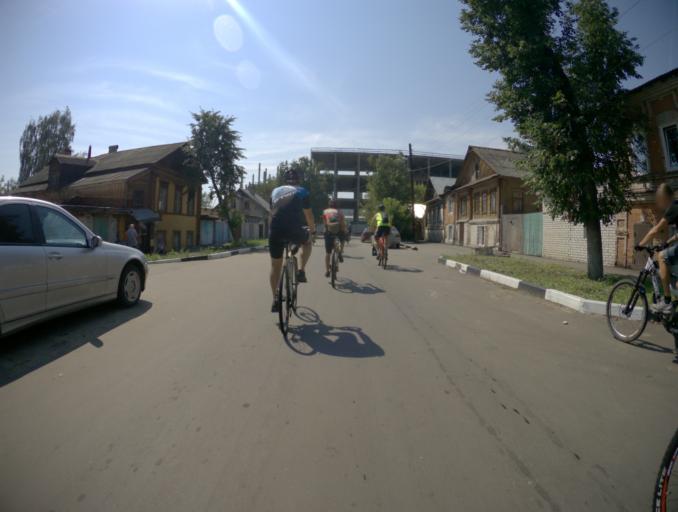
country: RU
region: Nizjnij Novgorod
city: Nizhniy Novgorod
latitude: 56.3173
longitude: 43.9492
